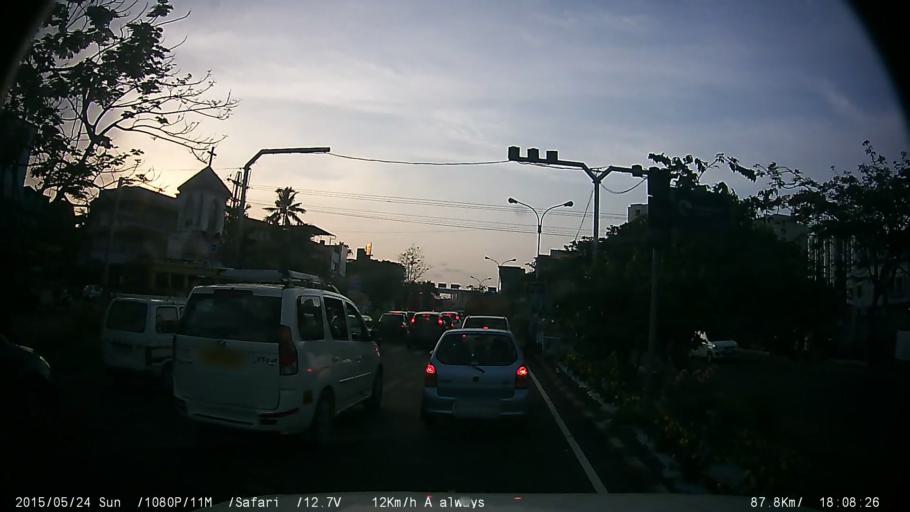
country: IN
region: Kerala
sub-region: Ernakulam
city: Elur
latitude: 10.0224
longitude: 76.3097
